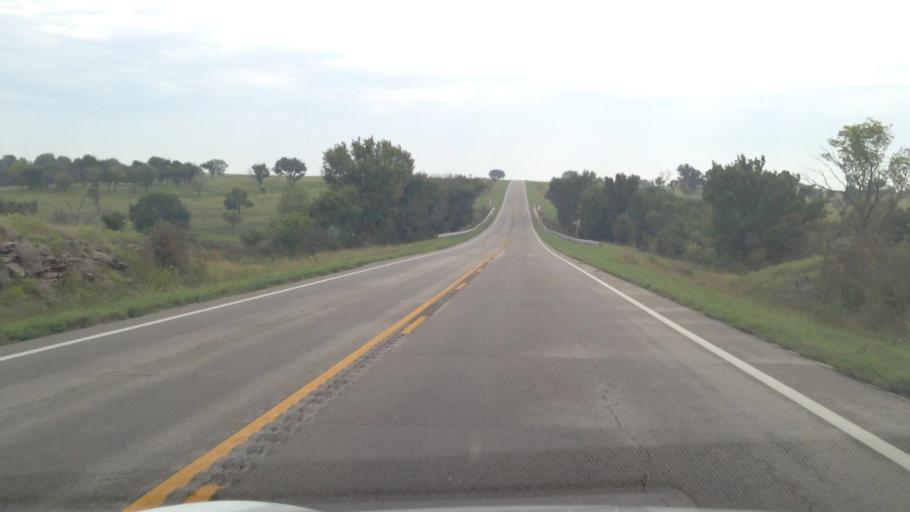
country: US
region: Kansas
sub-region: Bourbon County
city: Fort Scott
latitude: 37.8871
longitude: -95.0275
